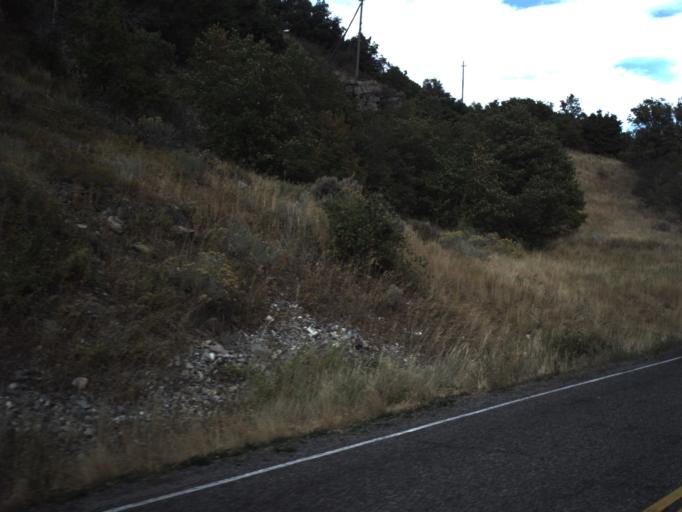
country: US
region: Utah
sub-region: Cache County
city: Millville
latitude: 41.6214
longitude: -111.7493
